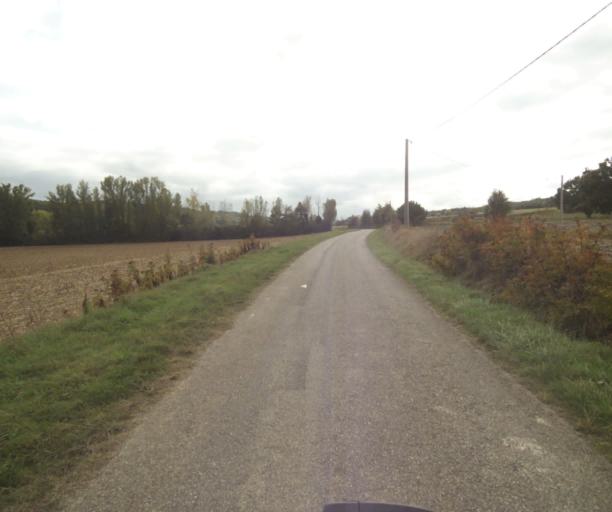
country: FR
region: Midi-Pyrenees
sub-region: Departement de la Haute-Garonne
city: Launac
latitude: 43.8436
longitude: 1.1125
